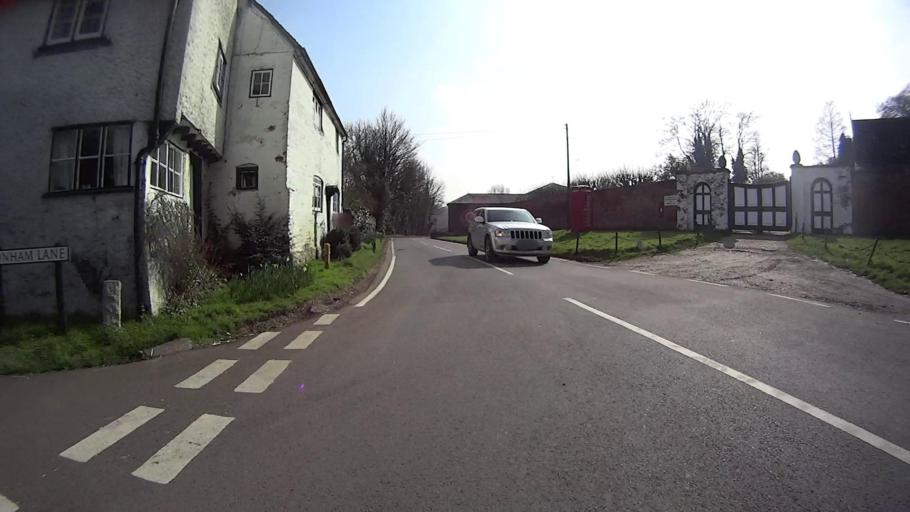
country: GB
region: England
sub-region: Surrey
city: Headley
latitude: 51.2334
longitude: -0.2662
